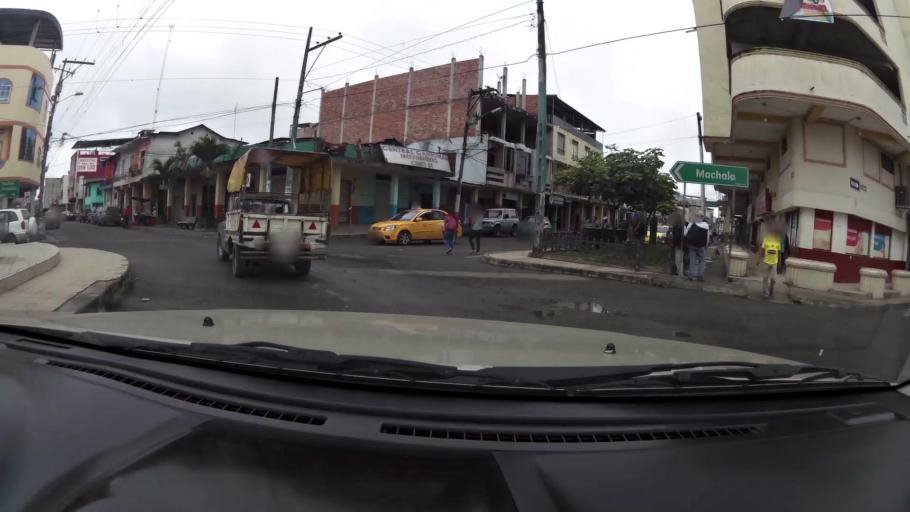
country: EC
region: El Oro
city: Pasaje
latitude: -3.3297
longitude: -79.8109
